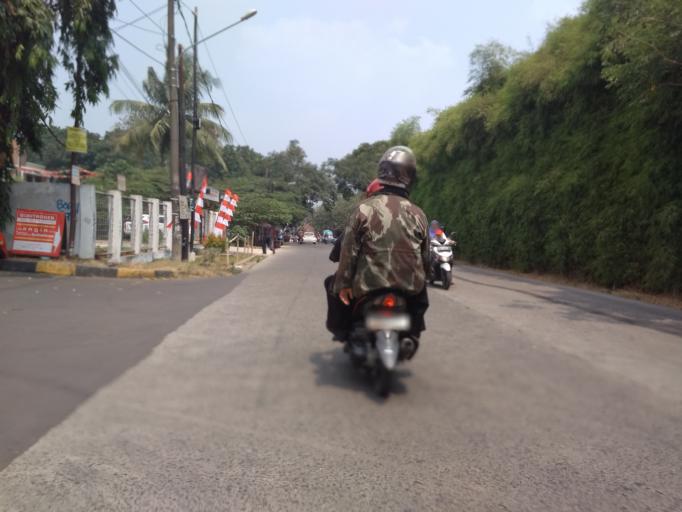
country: ID
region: West Java
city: Pamulang
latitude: -6.3182
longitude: 106.7891
